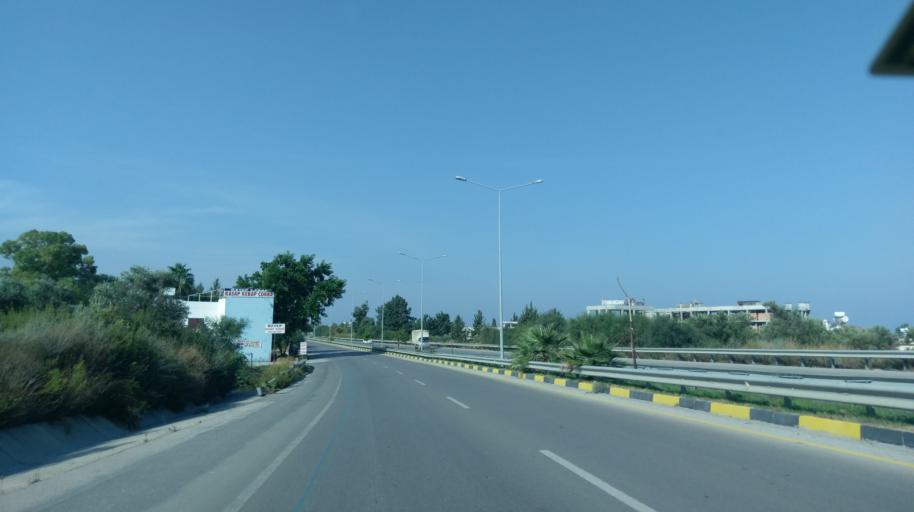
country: CY
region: Keryneia
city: Kyrenia
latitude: 35.3333
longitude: 33.2673
